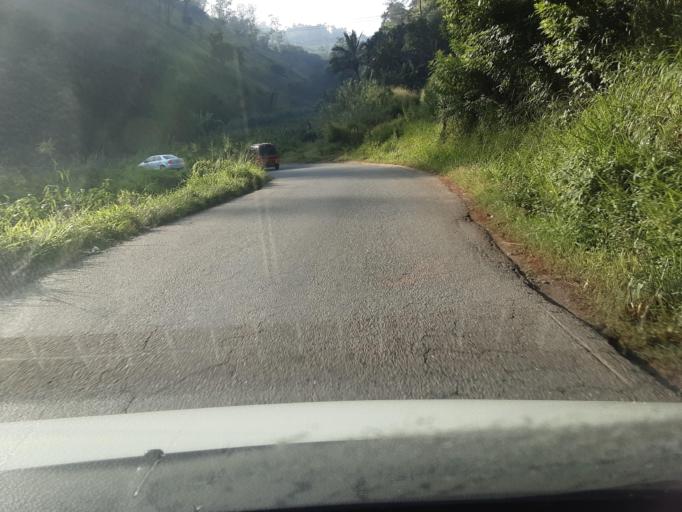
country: LK
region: Uva
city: Haputale
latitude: 6.9066
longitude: 80.9238
